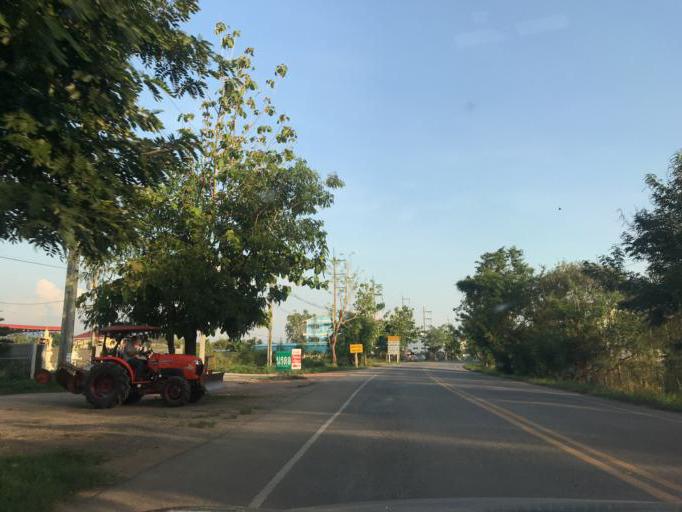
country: TH
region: Phayao
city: Chiang Kham
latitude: 19.5252
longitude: 100.2948
